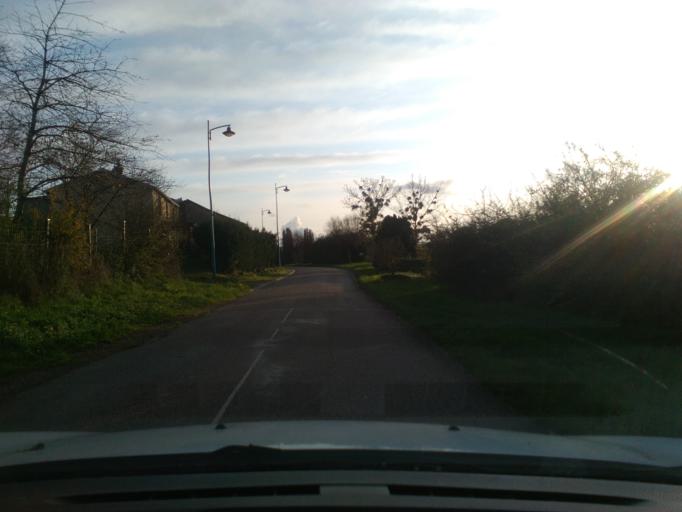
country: FR
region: Lorraine
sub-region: Departement des Vosges
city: Mirecourt
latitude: 48.2399
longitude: 6.1525
